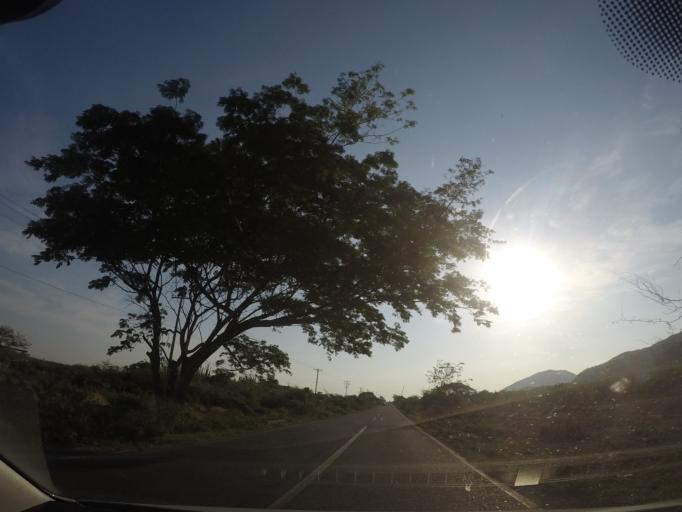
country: MX
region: Oaxaca
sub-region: Santo Domingo Tehuantepec
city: La Noria
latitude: 16.2311
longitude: -95.1773
